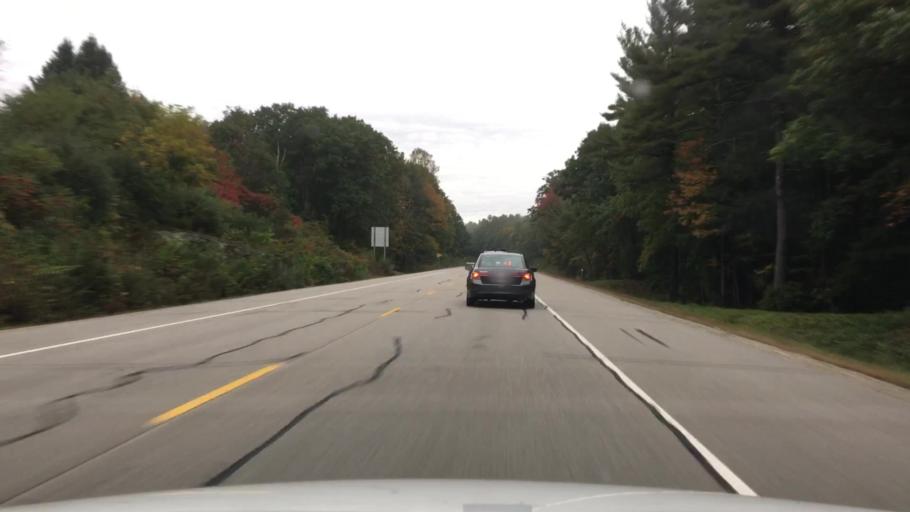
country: US
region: New Hampshire
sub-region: Strafford County
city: Durham
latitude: 43.1469
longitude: -70.9208
